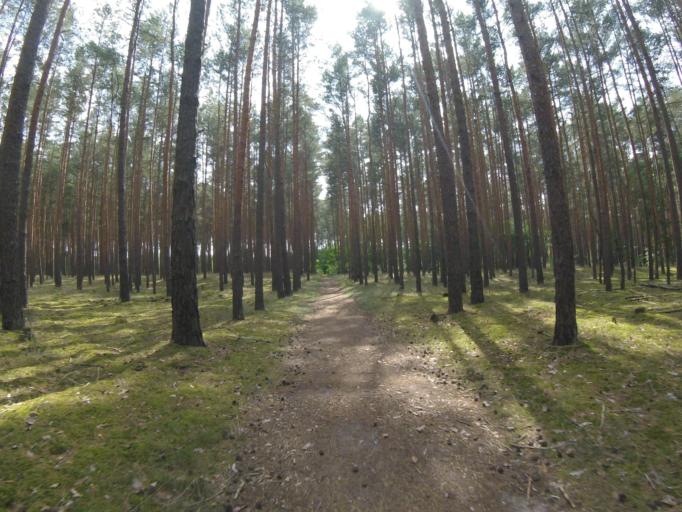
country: DE
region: Brandenburg
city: Bestensee
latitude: 52.2661
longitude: 13.6629
